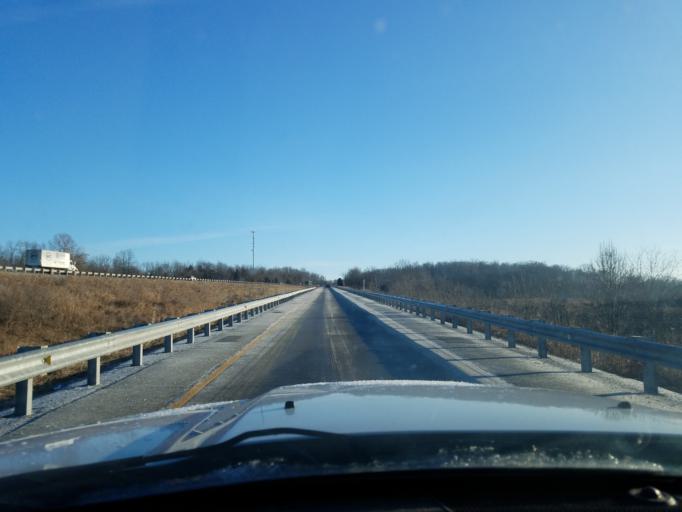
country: US
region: Kentucky
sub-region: Oldham County
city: Crestwood
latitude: 38.3468
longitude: -85.4899
